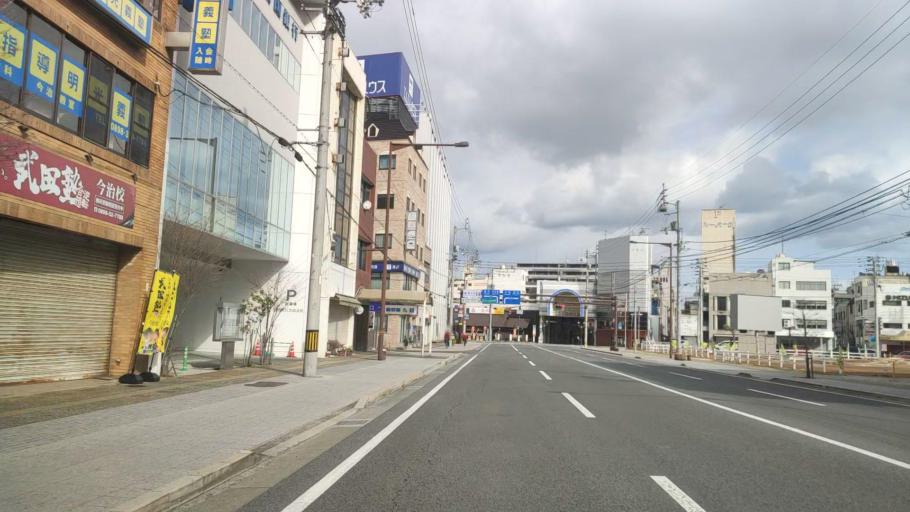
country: JP
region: Ehime
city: Saijo
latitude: 34.0647
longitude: 132.9983
